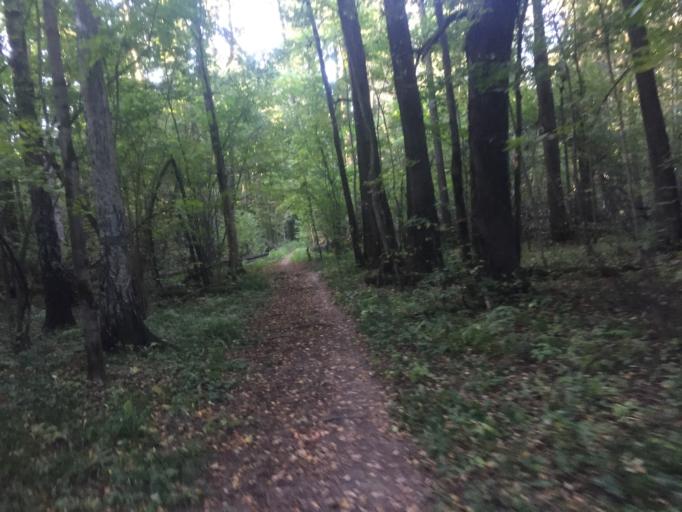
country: RU
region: Moscow
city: Gol'yanovo
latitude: 55.8463
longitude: 37.7877
